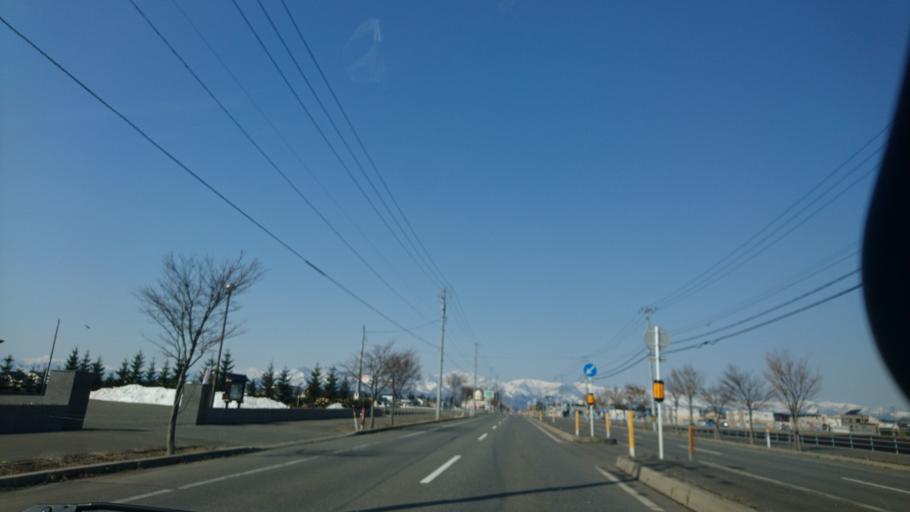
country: JP
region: Hokkaido
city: Obihiro
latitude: 42.9132
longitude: 143.0796
